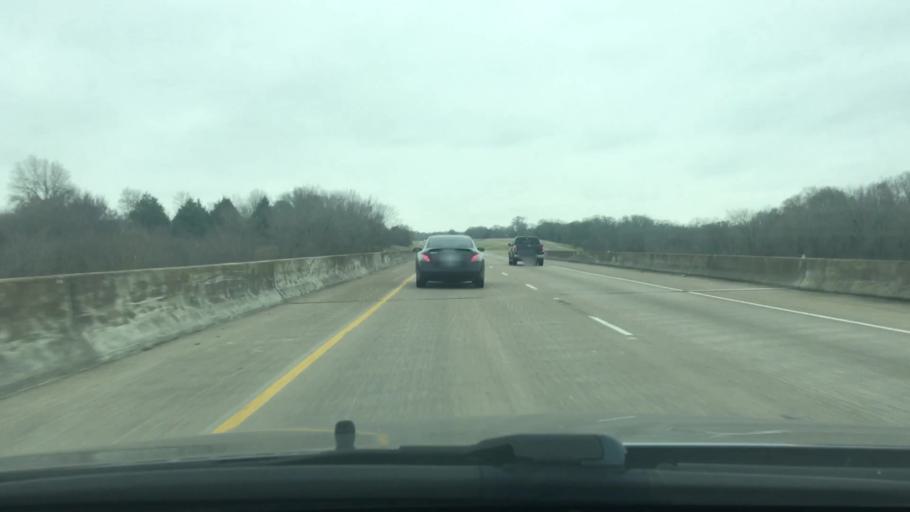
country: US
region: Texas
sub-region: Freestone County
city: Fairfield
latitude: 31.7961
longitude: -96.2540
